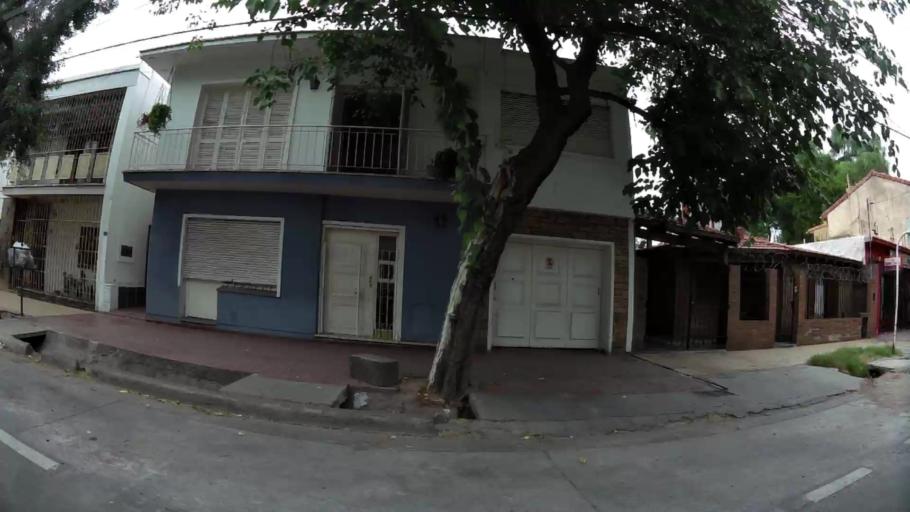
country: AR
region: Mendoza
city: Mendoza
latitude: -32.8943
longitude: -68.8590
